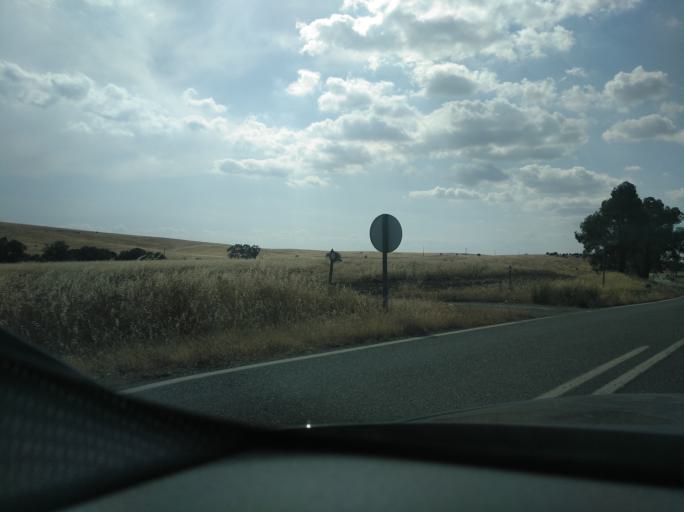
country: PT
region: Beja
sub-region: Mertola
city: Mertola
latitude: 37.7775
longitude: -7.8351
